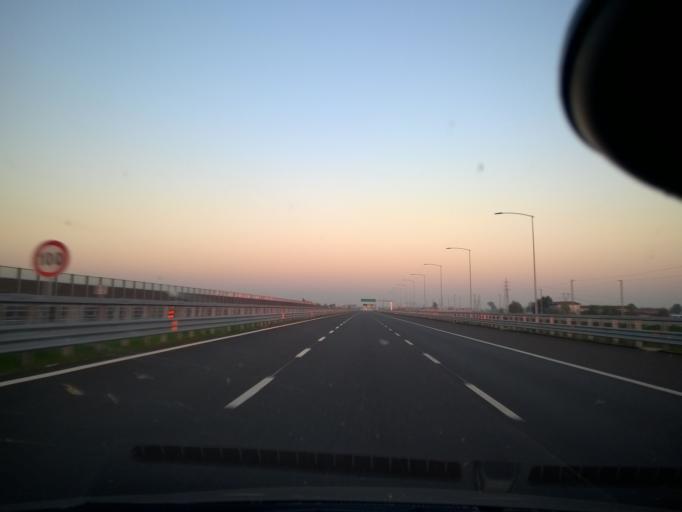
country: IT
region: Lombardy
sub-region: Provincia di Brescia
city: Castelcovati
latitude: 45.5202
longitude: 9.9461
